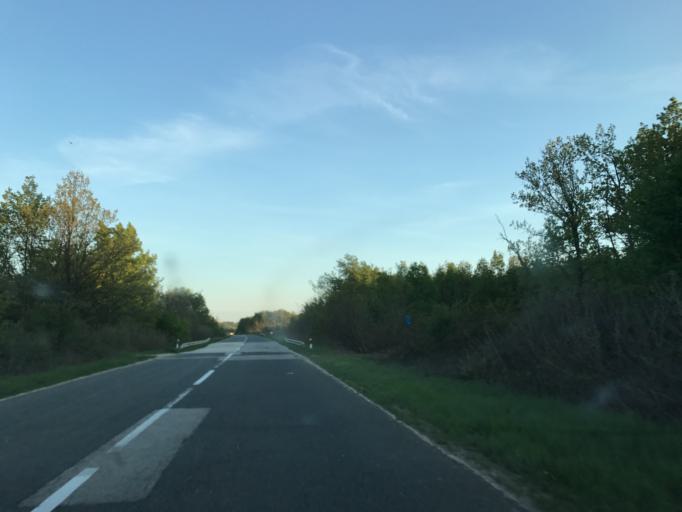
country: RO
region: Mehedinti
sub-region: Comuna Gogosu
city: Ostrovu Mare
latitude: 44.4467
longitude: 22.4543
